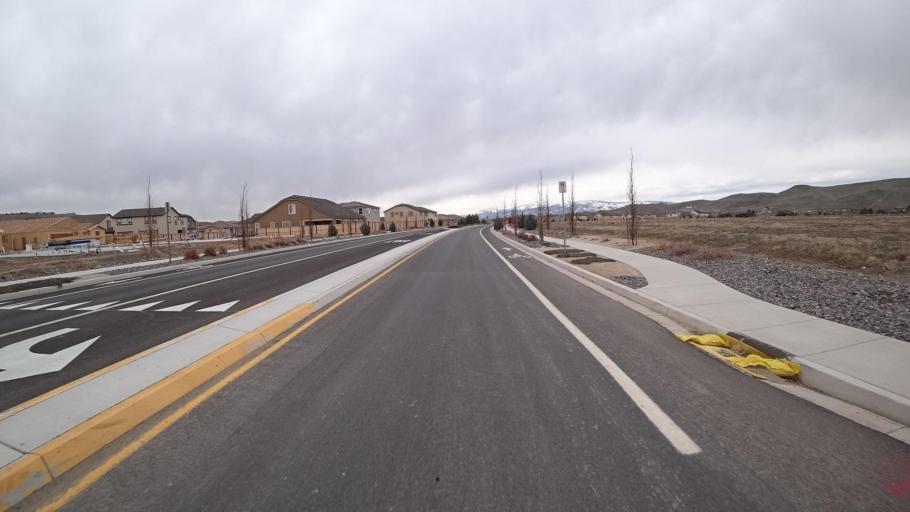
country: US
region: Nevada
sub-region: Washoe County
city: Spanish Springs
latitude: 39.6060
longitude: -119.7206
